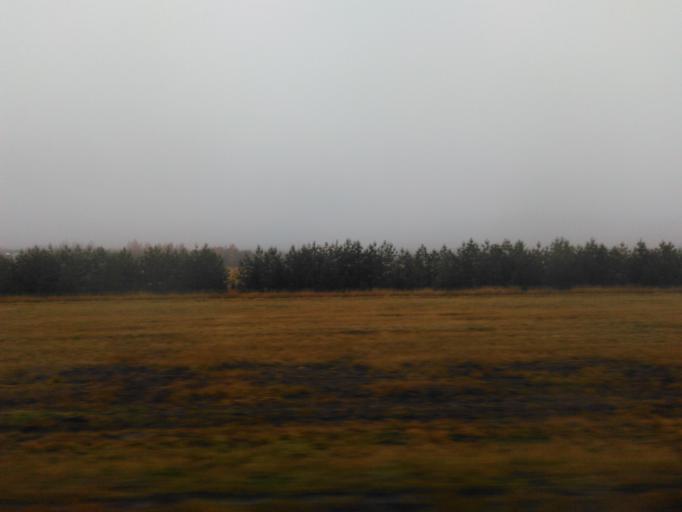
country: RU
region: Tatarstan
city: Sviyazhsk
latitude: 55.7345
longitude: 48.7784
